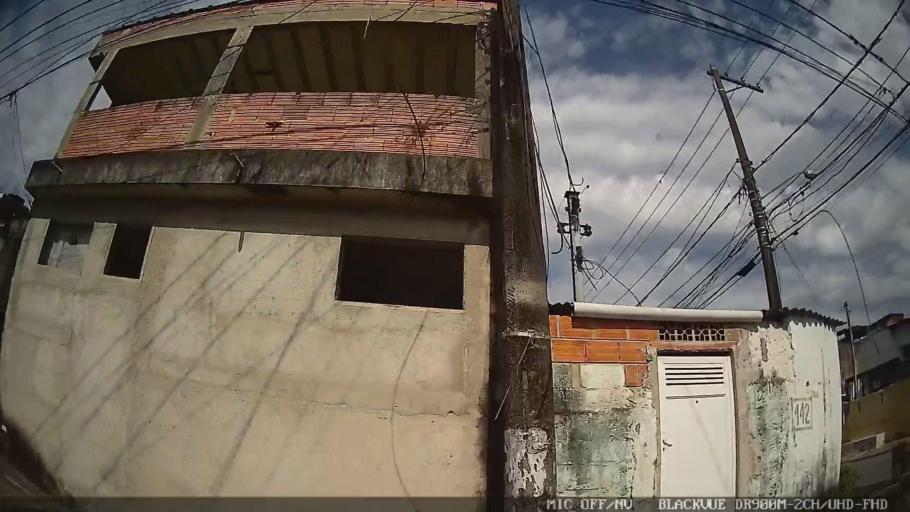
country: BR
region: Sao Paulo
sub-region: Santos
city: Santos
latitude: -23.9455
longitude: -46.2872
